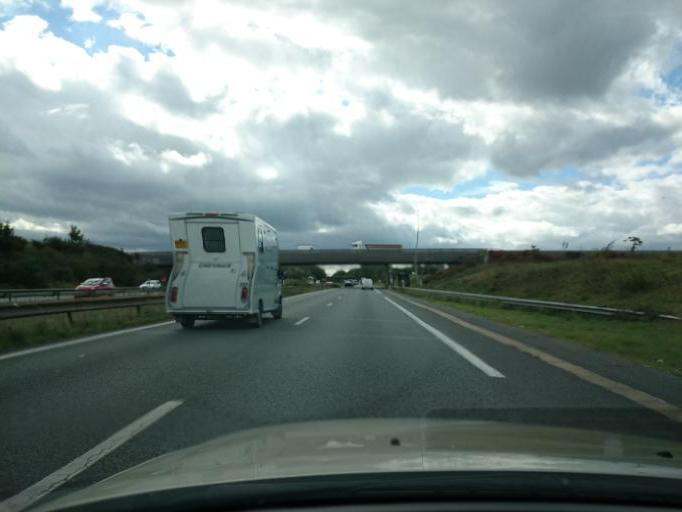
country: FR
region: Aquitaine
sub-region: Departement de la Gironde
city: Eysines
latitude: 44.8667
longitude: -0.6504
